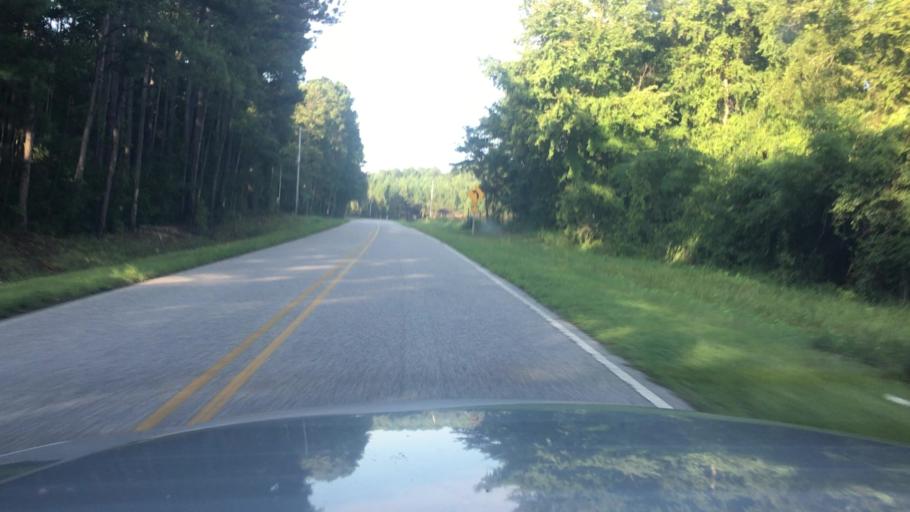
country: US
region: North Carolina
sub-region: Harnett County
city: Walkertown
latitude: 35.2247
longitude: -78.8913
